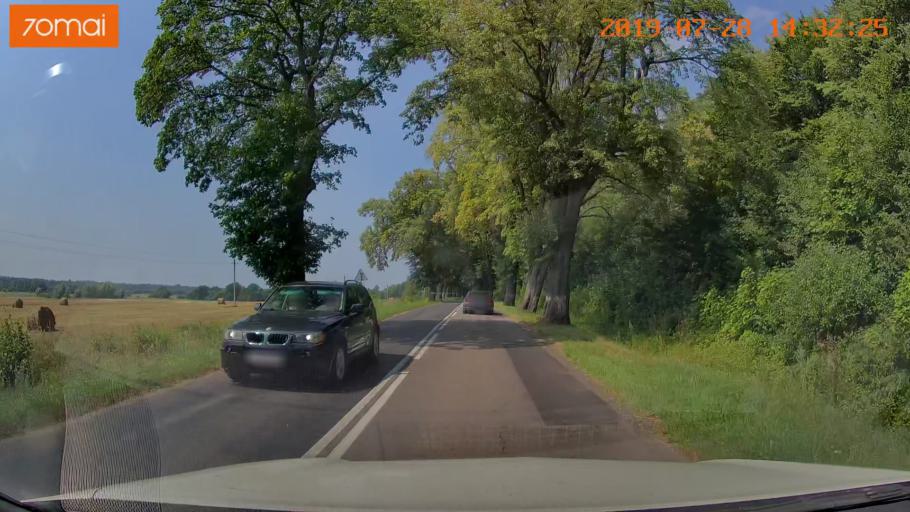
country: RU
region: Kaliningrad
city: Primorsk
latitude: 54.8126
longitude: 20.0417
